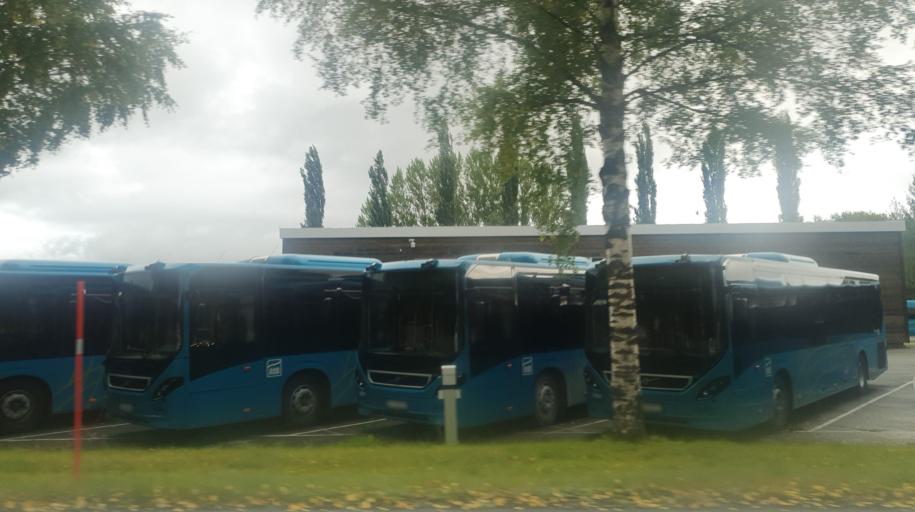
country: NO
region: Nord-Trondelag
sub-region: Verdal
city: Verdal
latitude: 63.7952
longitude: 11.5004
